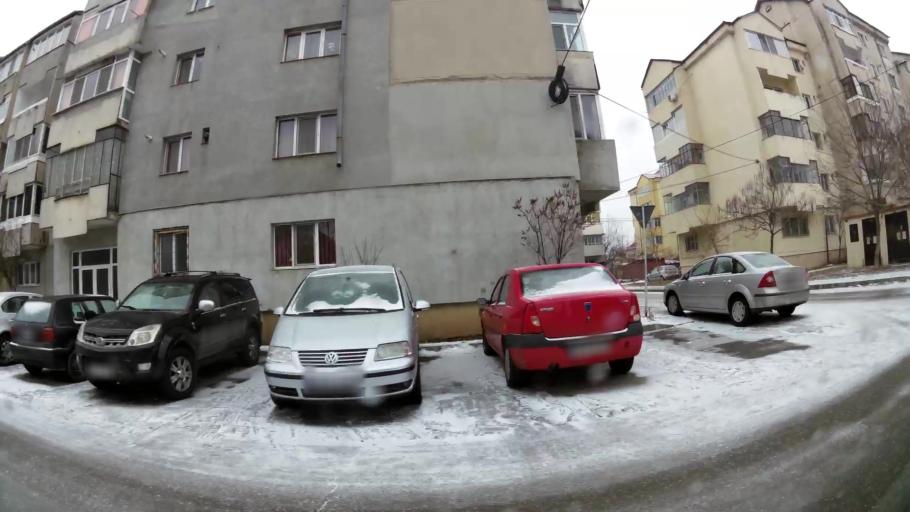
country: RO
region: Dambovita
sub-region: Municipiul Targoviste
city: Targoviste
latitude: 44.9359
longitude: 25.4434
